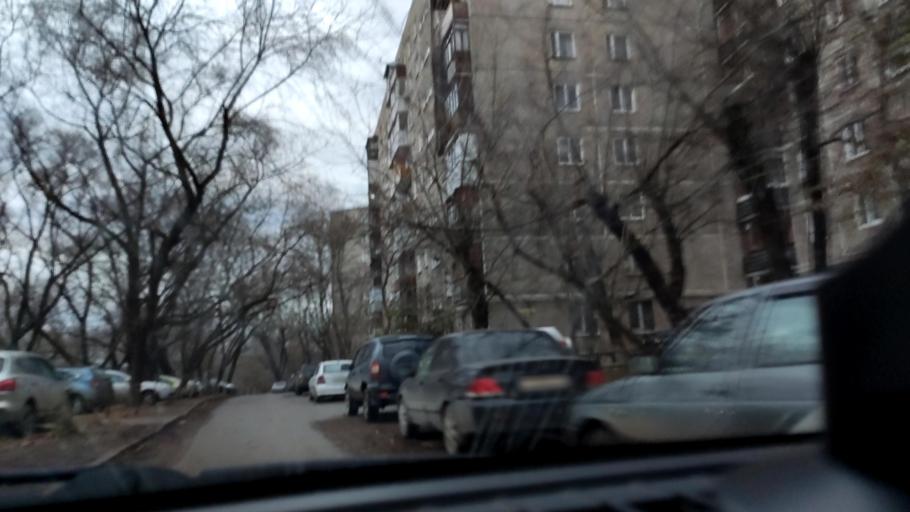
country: RU
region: Perm
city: Perm
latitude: 57.9778
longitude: 56.2751
